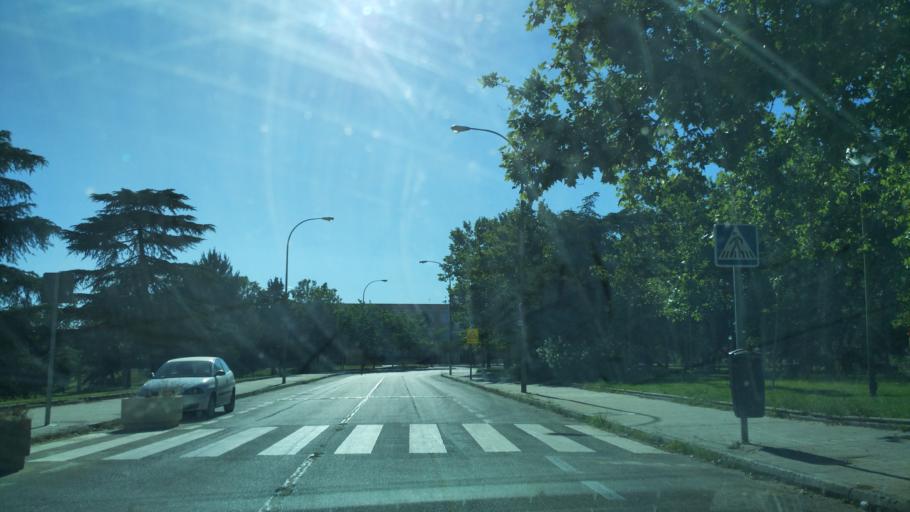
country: ES
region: Madrid
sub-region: Provincia de Madrid
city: Tetuan de las Victorias
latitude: 40.4742
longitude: -3.7081
